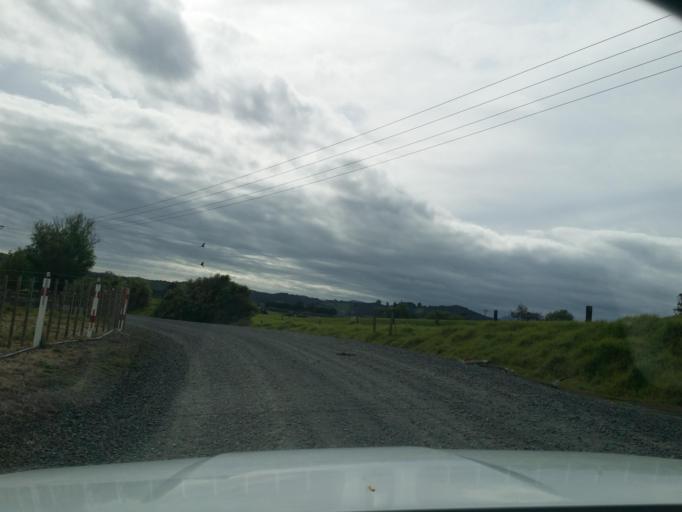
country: NZ
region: Northland
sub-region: Kaipara District
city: Dargaville
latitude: -35.8941
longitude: 173.9110
